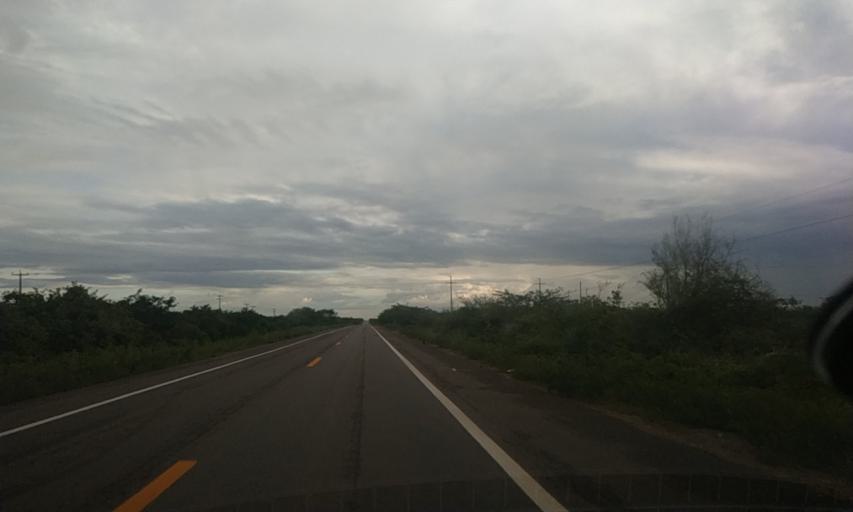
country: BR
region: Rio Grande do Norte
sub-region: Mossoro
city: Mossoro
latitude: -5.1365
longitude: -37.2112
